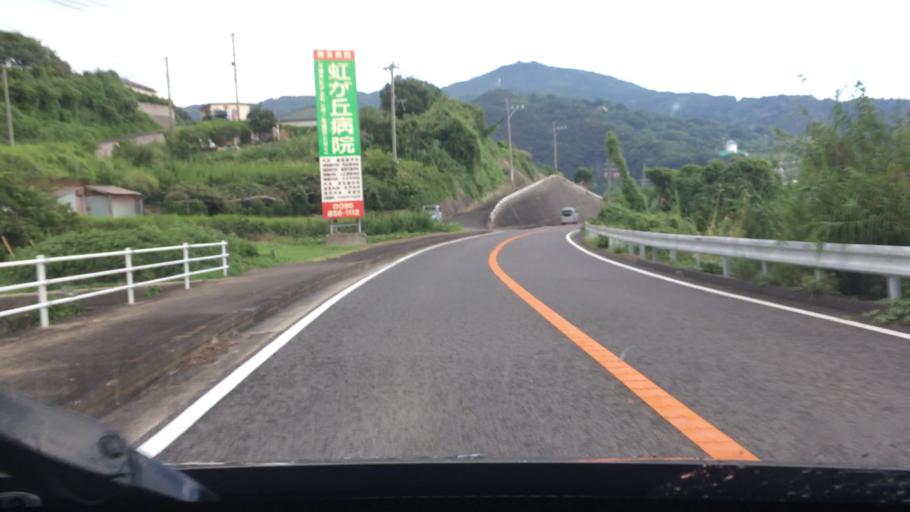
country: JP
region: Nagasaki
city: Togitsu
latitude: 32.8842
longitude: 129.6782
